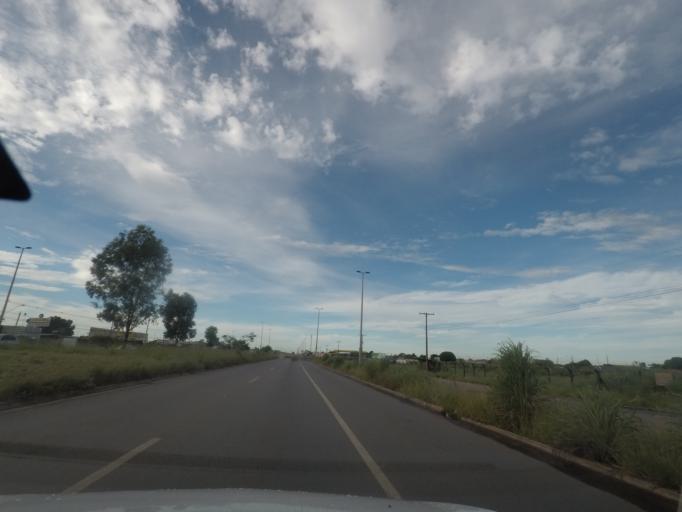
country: BR
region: Goias
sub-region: Aparecida De Goiania
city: Aparecida de Goiania
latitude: -16.7769
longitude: -49.3526
